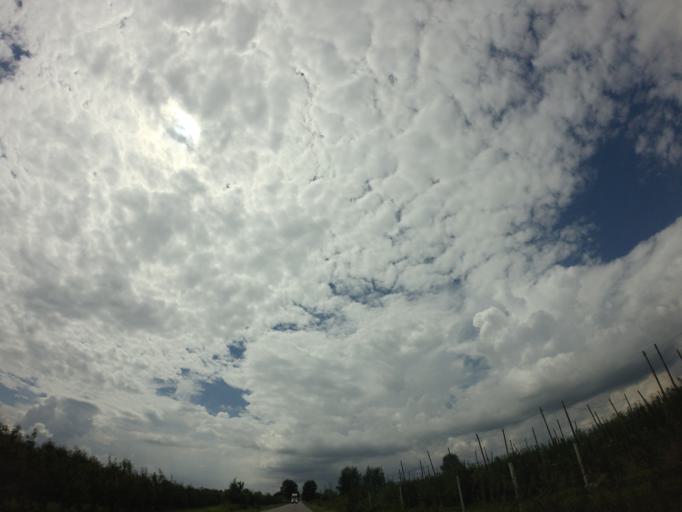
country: PL
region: Lublin Voivodeship
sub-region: Powiat opolski
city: Wilkow
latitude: 51.2428
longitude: 21.8571
